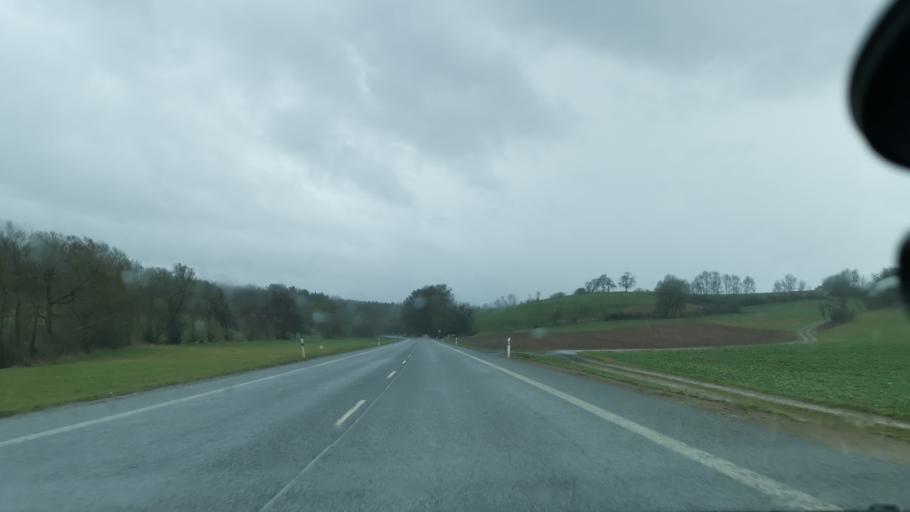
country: DE
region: Hesse
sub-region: Regierungsbezirk Kassel
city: Cornberg
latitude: 51.0534
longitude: 9.8791
